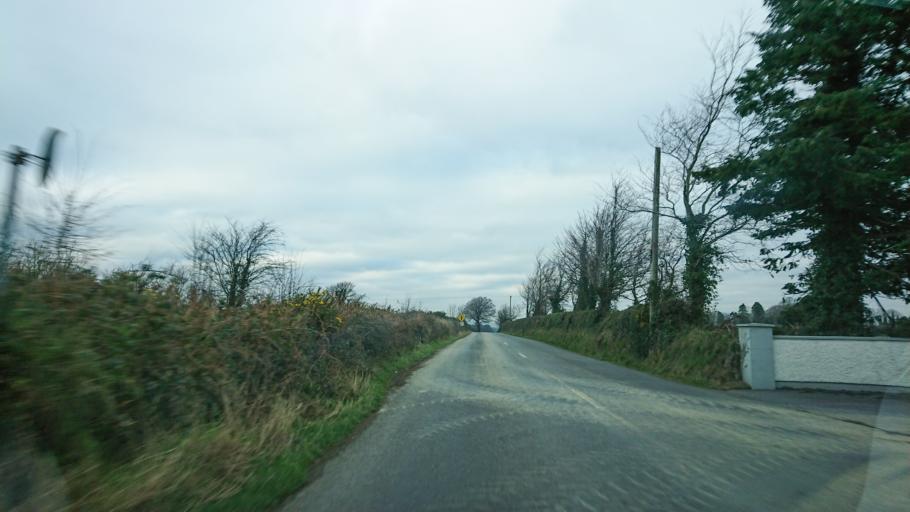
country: IE
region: Munster
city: Carrick-on-Suir
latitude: 52.2943
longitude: -7.4695
